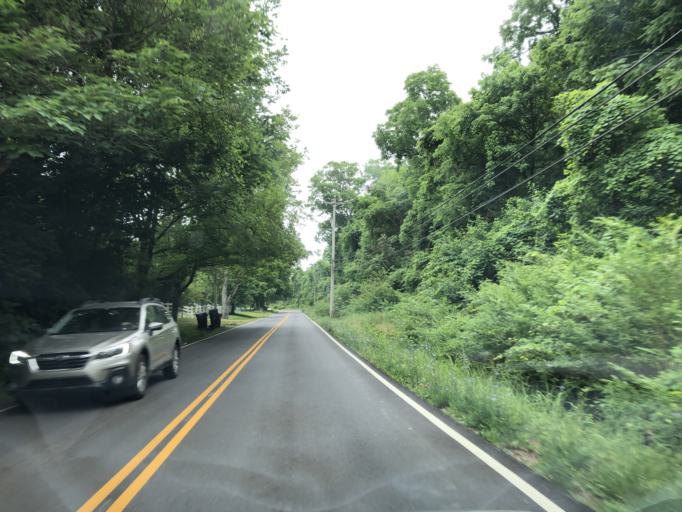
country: US
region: Tennessee
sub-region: Davidson County
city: Goodlettsville
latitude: 36.2942
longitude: -86.7475
